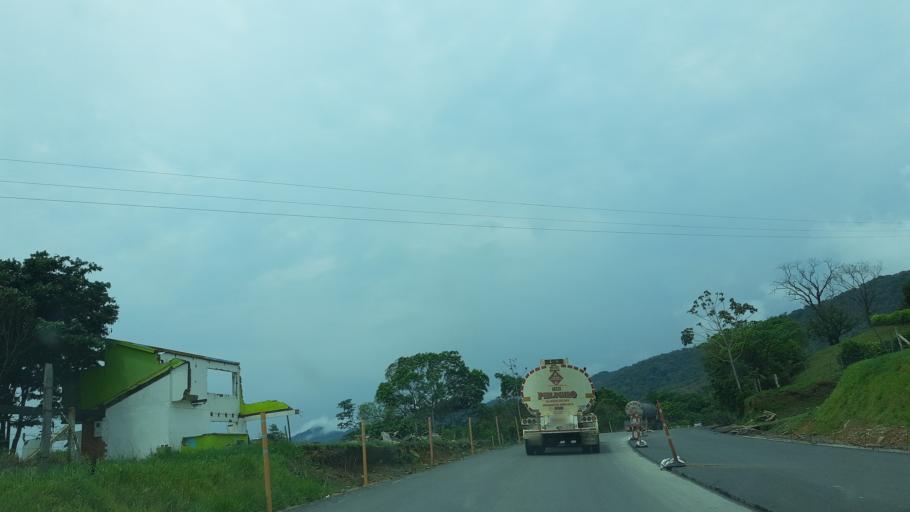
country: CO
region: Casanare
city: Sabanalarga
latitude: 4.7910
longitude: -72.9900
